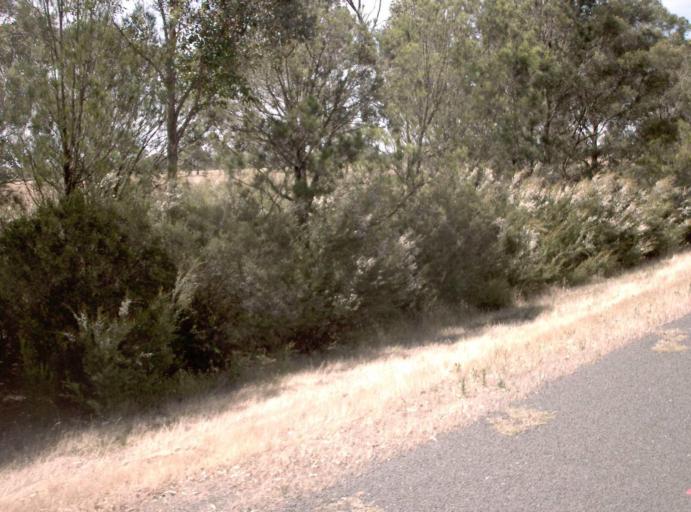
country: AU
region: Victoria
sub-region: Wellington
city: Sale
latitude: -37.9390
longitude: 147.1505
